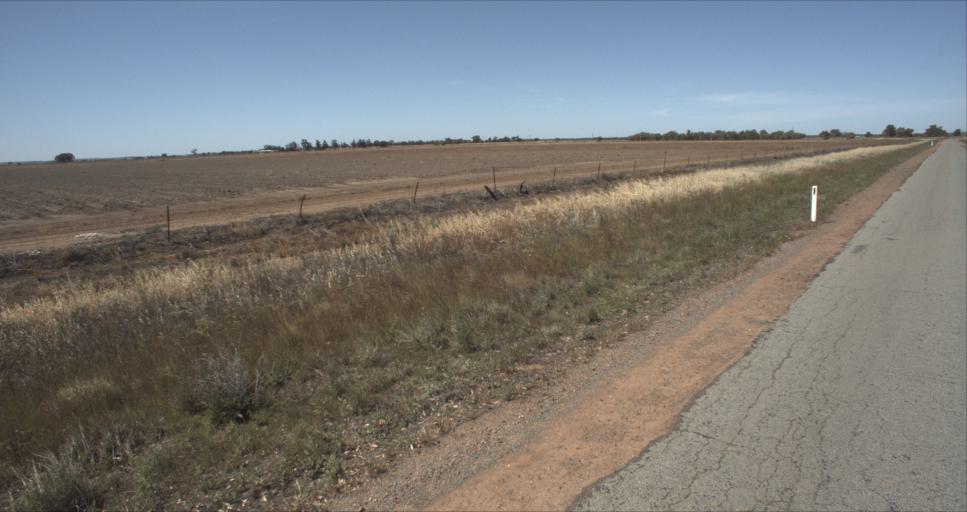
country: AU
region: New South Wales
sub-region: Leeton
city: Leeton
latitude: -34.5629
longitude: 146.3124
